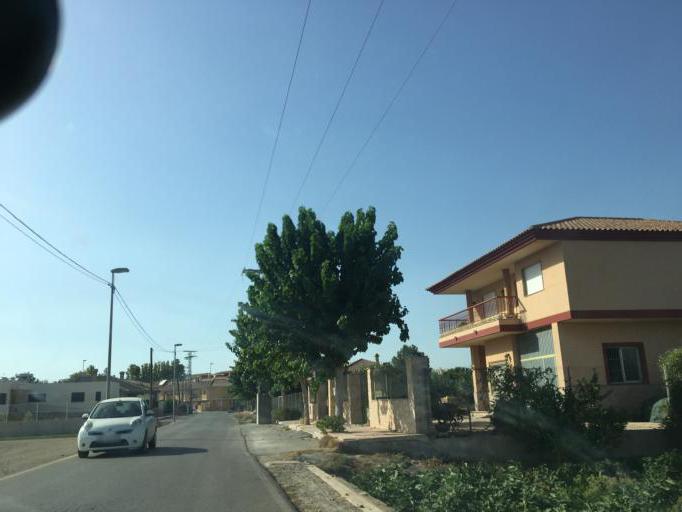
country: ES
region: Murcia
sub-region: Murcia
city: Santomera
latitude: 38.0354
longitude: -1.0736
